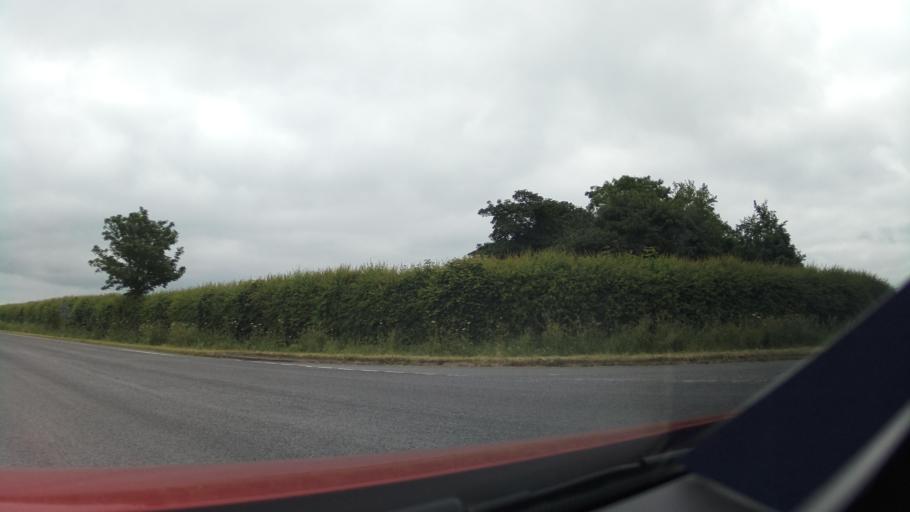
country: GB
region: England
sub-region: District of Rutland
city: Ridlington
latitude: 52.5991
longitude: -0.7428
